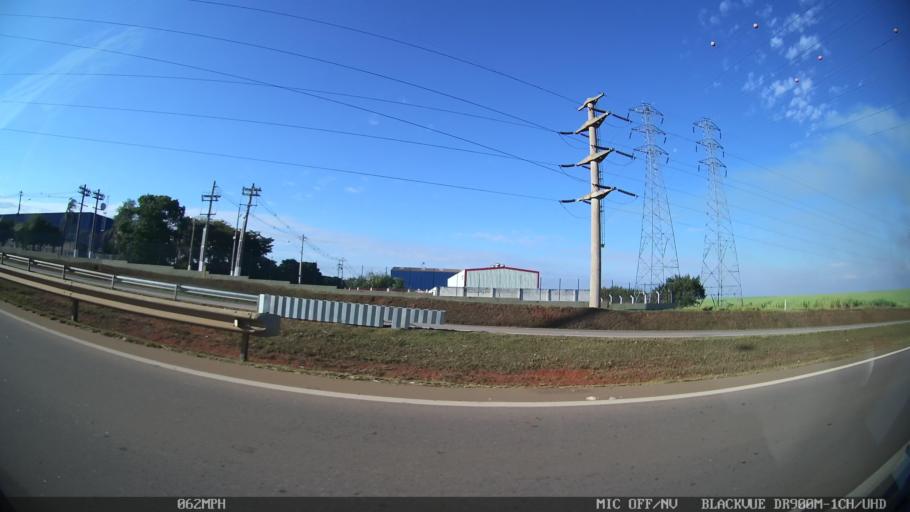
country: BR
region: Sao Paulo
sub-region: Piracicaba
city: Piracicaba
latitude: -22.6711
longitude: -47.6026
